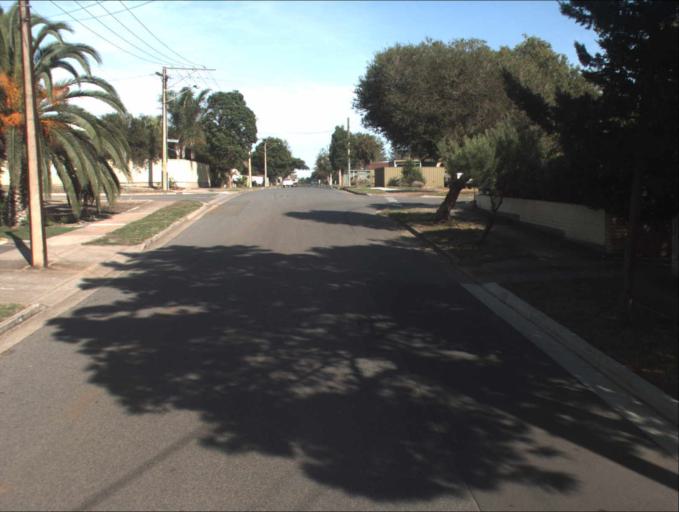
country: AU
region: South Australia
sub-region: Port Adelaide Enfield
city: Birkenhead
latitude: -34.8076
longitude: 138.4959
